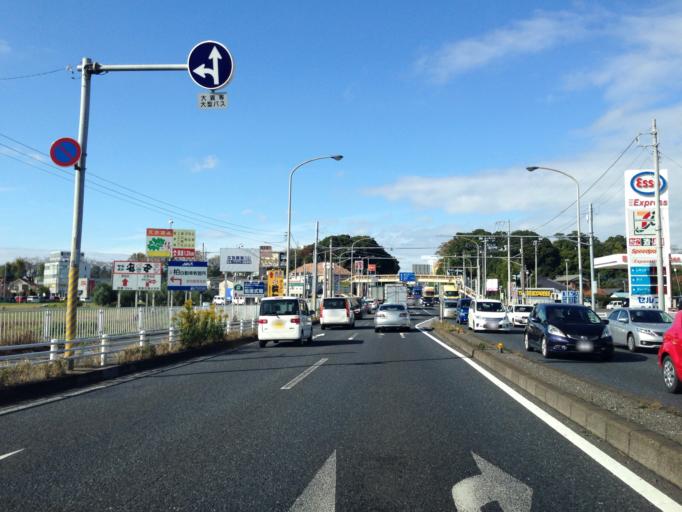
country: JP
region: Chiba
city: Kashiwa
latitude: 35.8728
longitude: 139.9722
